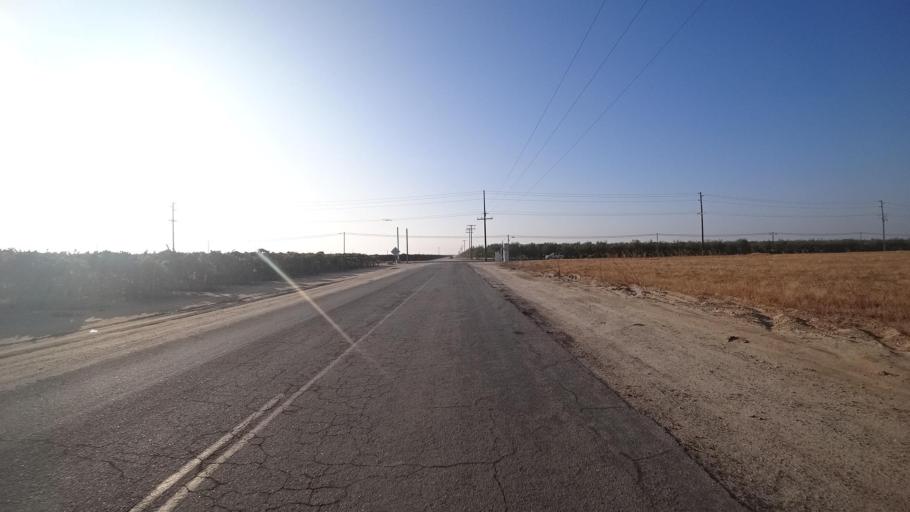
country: US
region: California
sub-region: Tulare County
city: Richgrove
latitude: 35.7770
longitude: -119.1340
